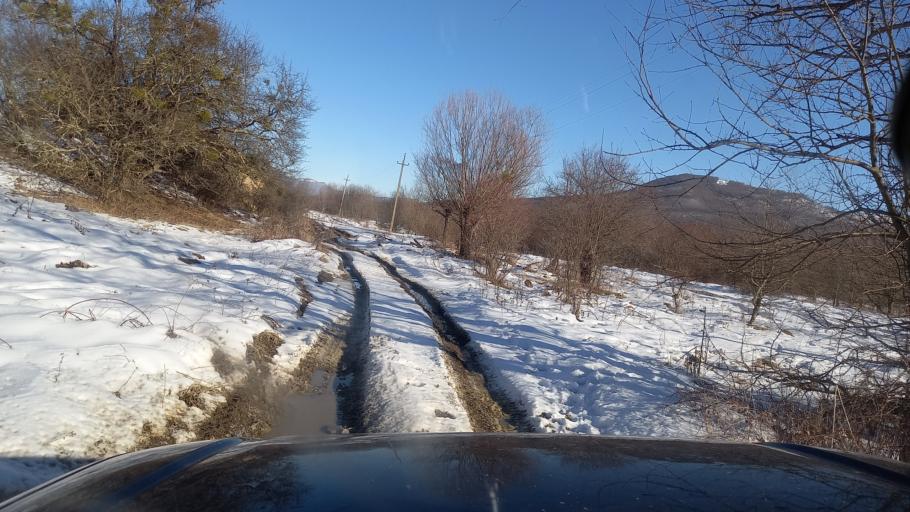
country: RU
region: Adygeya
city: Kamennomostskiy
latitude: 44.2046
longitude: 40.1527
